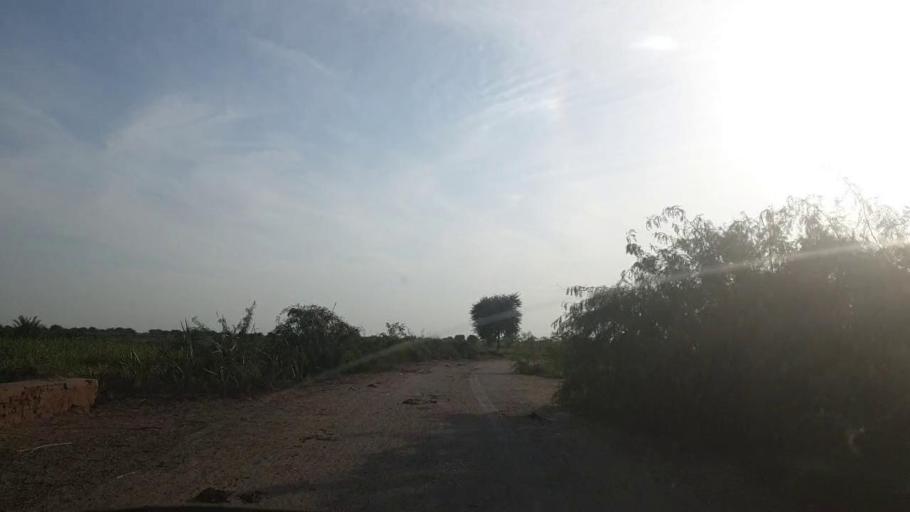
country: PK
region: Sindh
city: Tando Muhammad Khan
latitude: 25.2185
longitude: 68.5222
